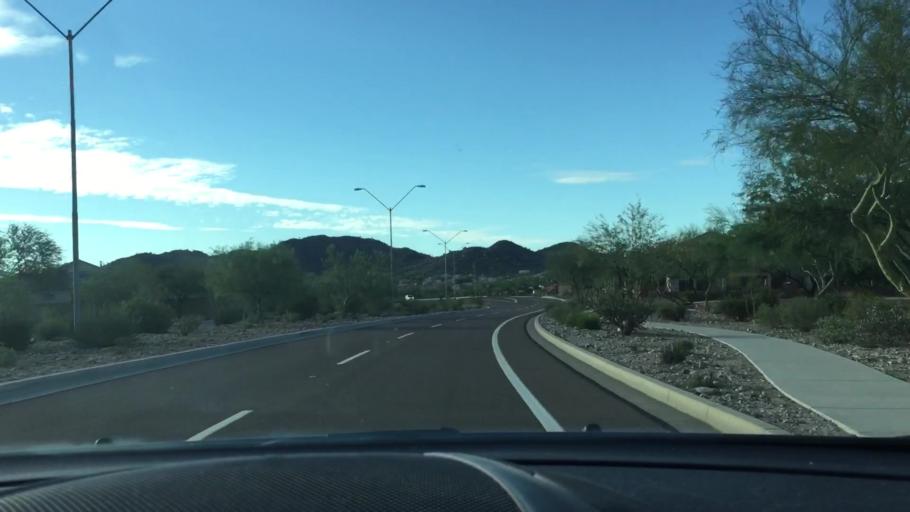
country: US
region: Arizona
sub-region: Maricopa County
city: Sun City West
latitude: 33.7343
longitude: -112.2539
